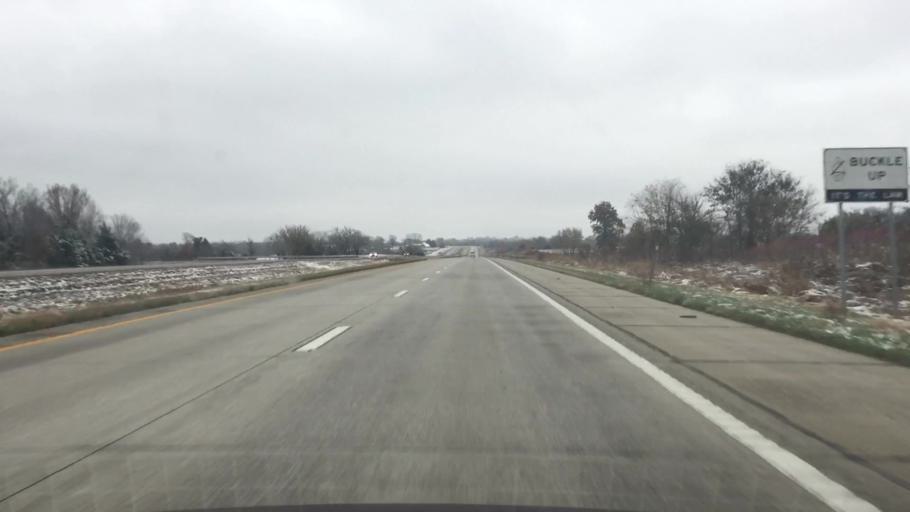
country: US
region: Missouri
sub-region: Saint Clair County
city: Osceola
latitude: 38.2019
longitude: -93.7498
